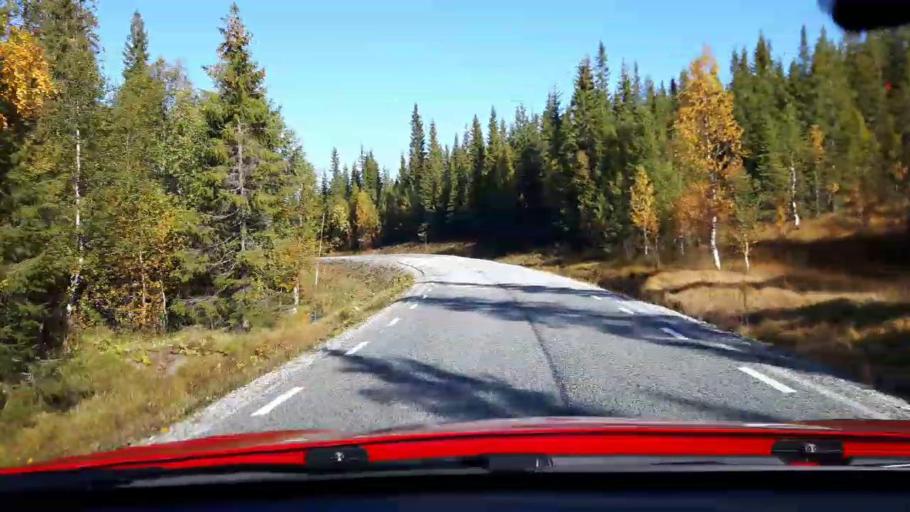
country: NO
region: Nord-Trondelag
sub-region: Lierne
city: Sandvika
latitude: 64.6173
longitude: 13.7009
